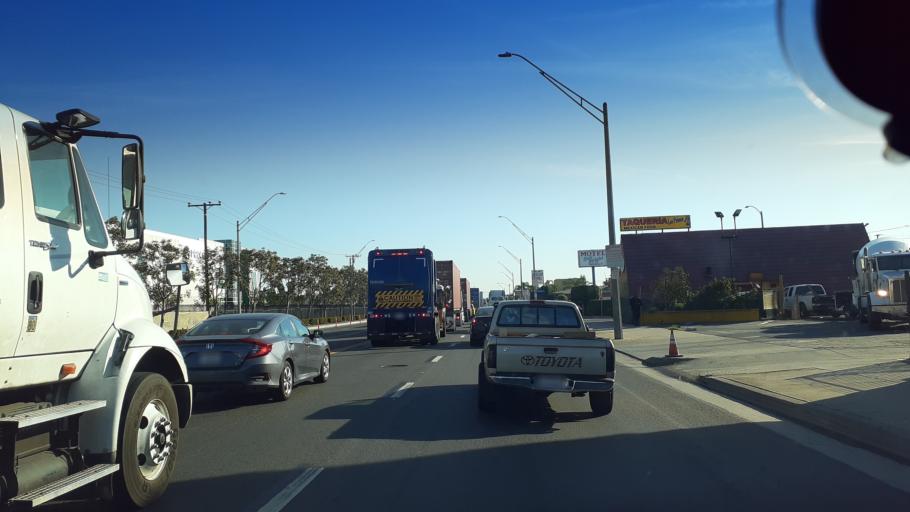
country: US
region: California
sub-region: Los Angeles County
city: Long Beach
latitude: 33.7898
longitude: -118.2184
